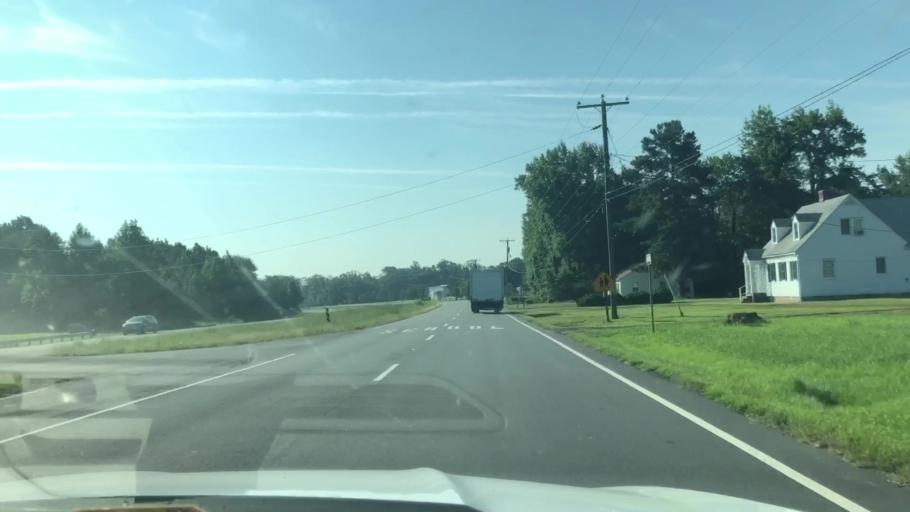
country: US
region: Virginia
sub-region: Richmond County
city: Warsaw
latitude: 37.9366
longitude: -76.7427
